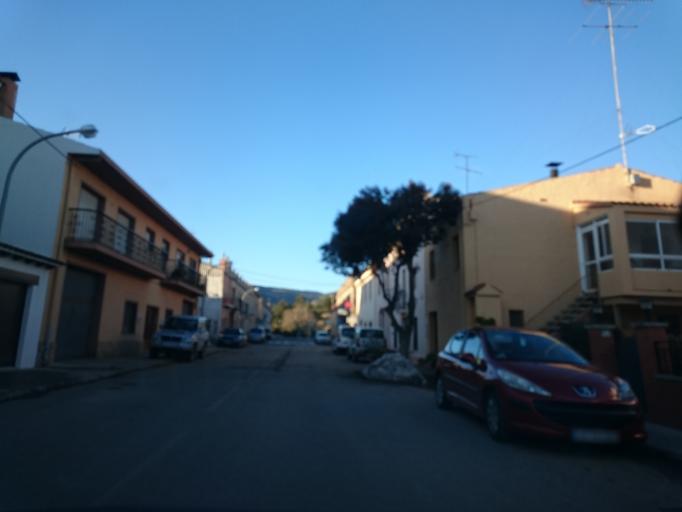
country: ES
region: Catalonia
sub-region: Provincia de Tarragona
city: la Bisbal del Penedes
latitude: 41.3670
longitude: 1.5016
